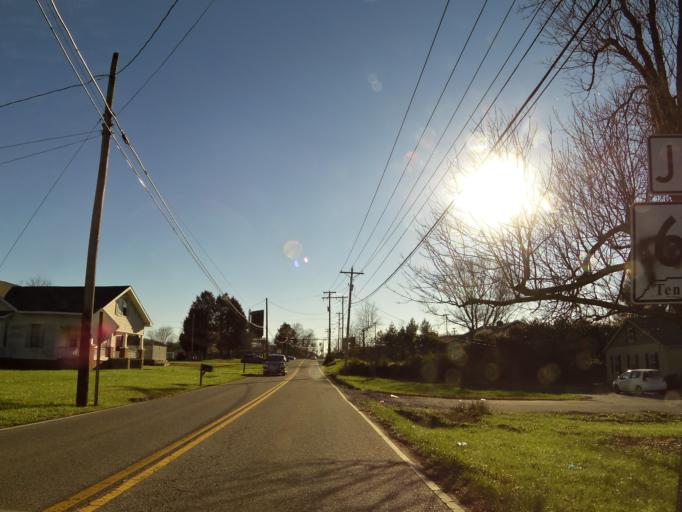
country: US
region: Tennessee
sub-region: Knox County
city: Farragut
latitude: 35.9808
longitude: -84.1143
